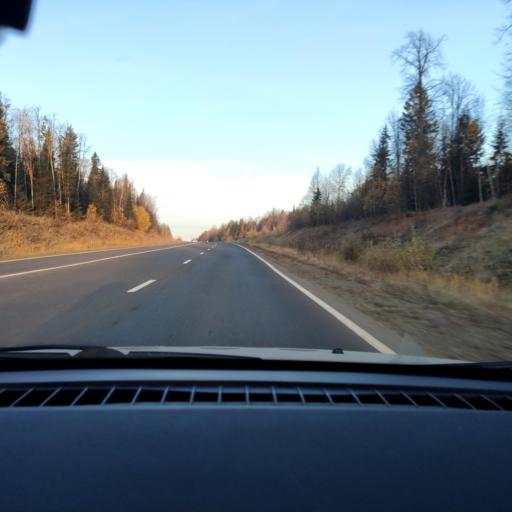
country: RU
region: Perm
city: Novyye Lyady
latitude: 58.0403
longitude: 56.4604
